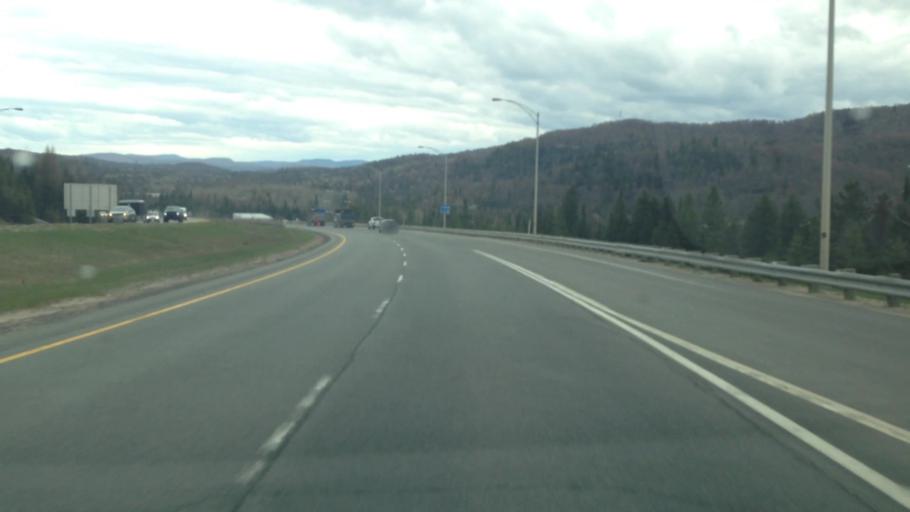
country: CA
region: Quebec
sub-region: Laurentides
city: Sainte-Agathe-des-Monts
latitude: 46.0463
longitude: -74.2657
